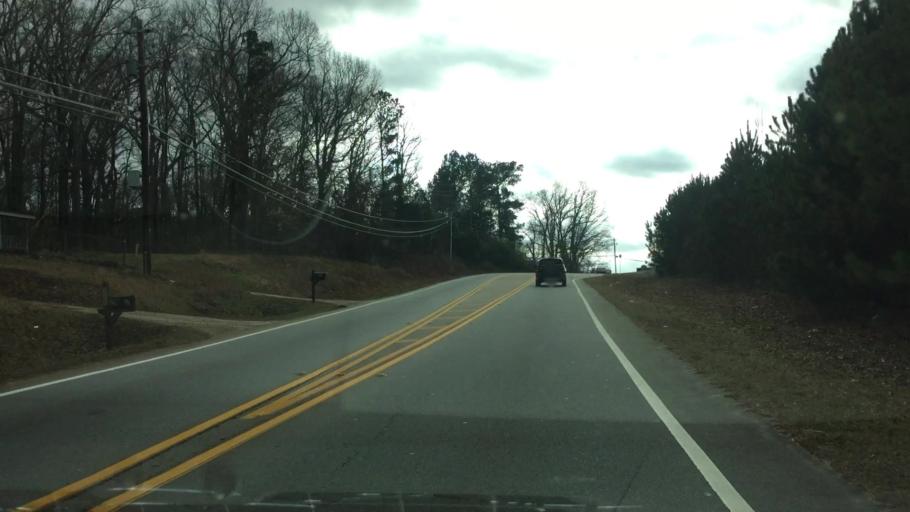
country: US
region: Georgia
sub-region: Henry County
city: McDonough
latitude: 33.4389
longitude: -84.1568
